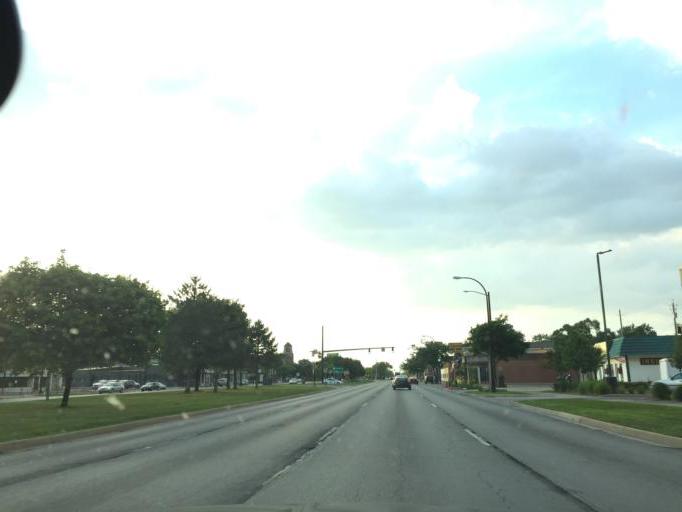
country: US
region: Michigan
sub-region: Oakland County
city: Ferndale
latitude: 42.4537
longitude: -83.1296
